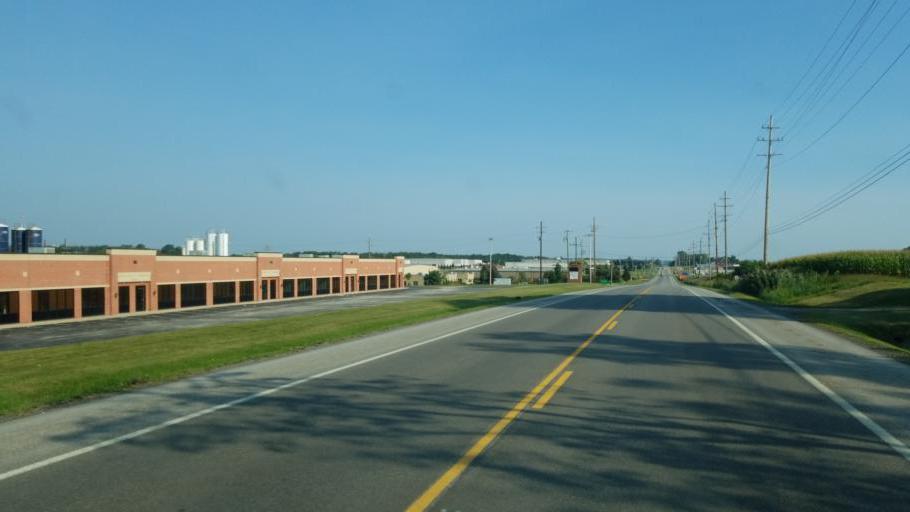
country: US
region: Ohio
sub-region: Geauga County
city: Middlefield
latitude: 41.4548
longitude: -81.0513
